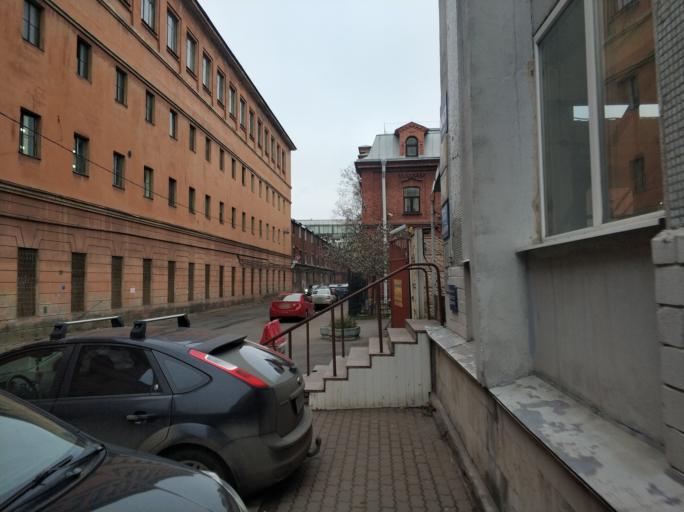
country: RU
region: Leningrad
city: Sampsonievskiy
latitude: 59.9708
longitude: 30.3378
